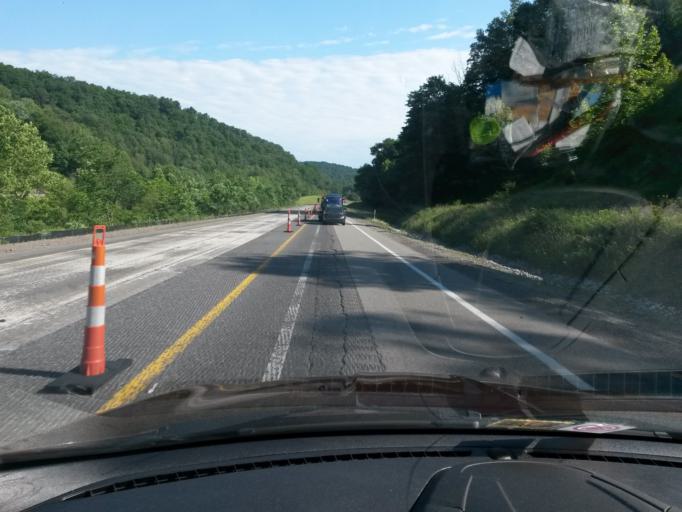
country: US
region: West Virginia
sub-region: Braxton County
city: Sutton
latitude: 38.7467
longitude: -80.6761
